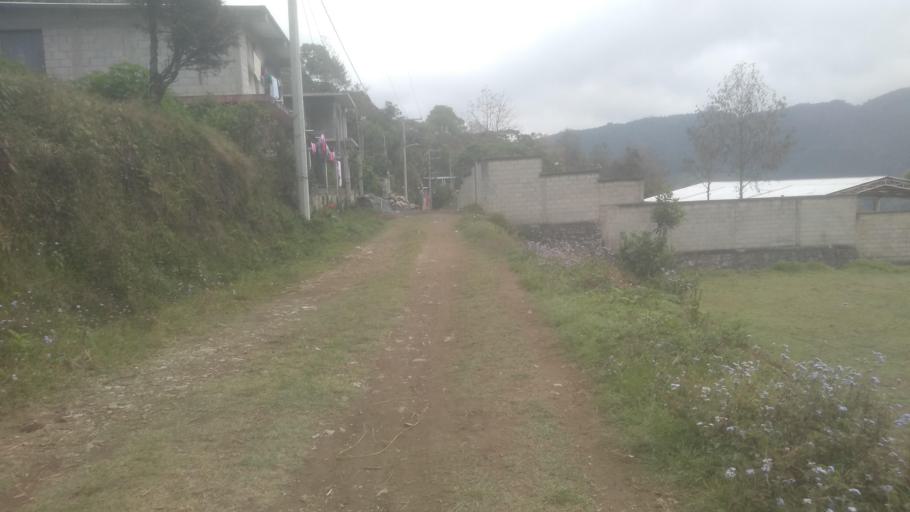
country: MX
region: Veracruz
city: Chocaman
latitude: 18.9886
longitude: -97.0578
